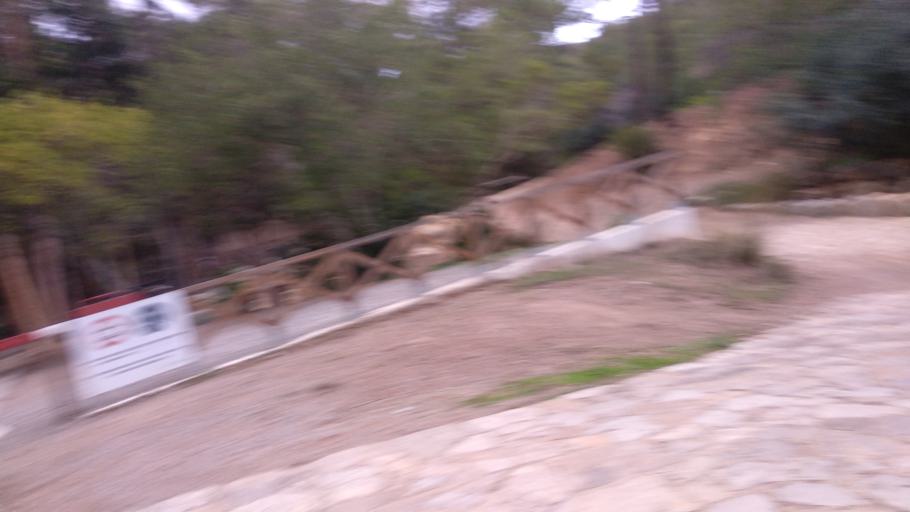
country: PT
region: Faro
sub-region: Sao Bras de Alportel
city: Sao Bras de Alportel
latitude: 37.1851
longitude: -7.9142
